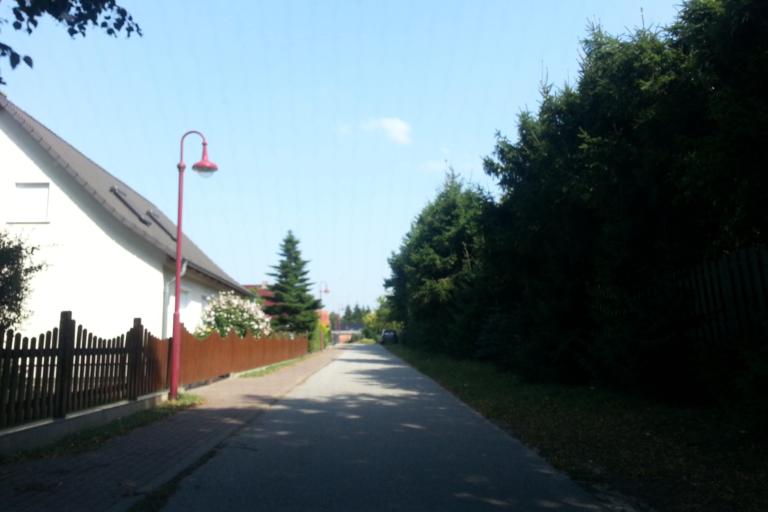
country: DE
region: Mecklenburg-Vorpommern
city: Ferdinandshof
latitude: 53.5960
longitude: 13.8121
